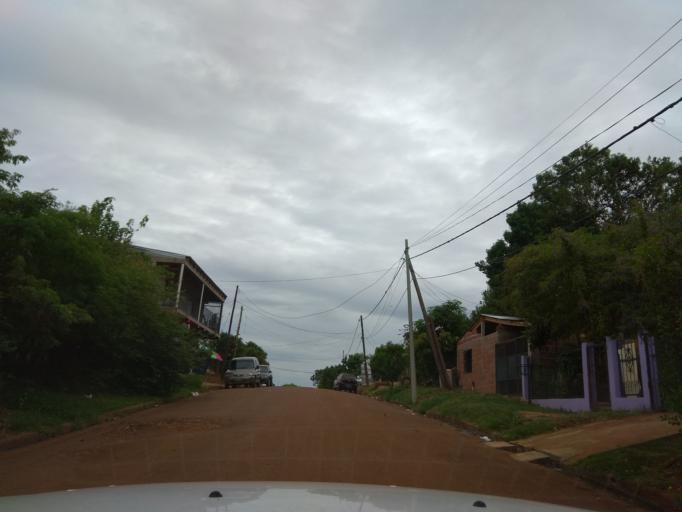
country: AR
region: Misiones
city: Garupa
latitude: -27.4391
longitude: -55.8621
